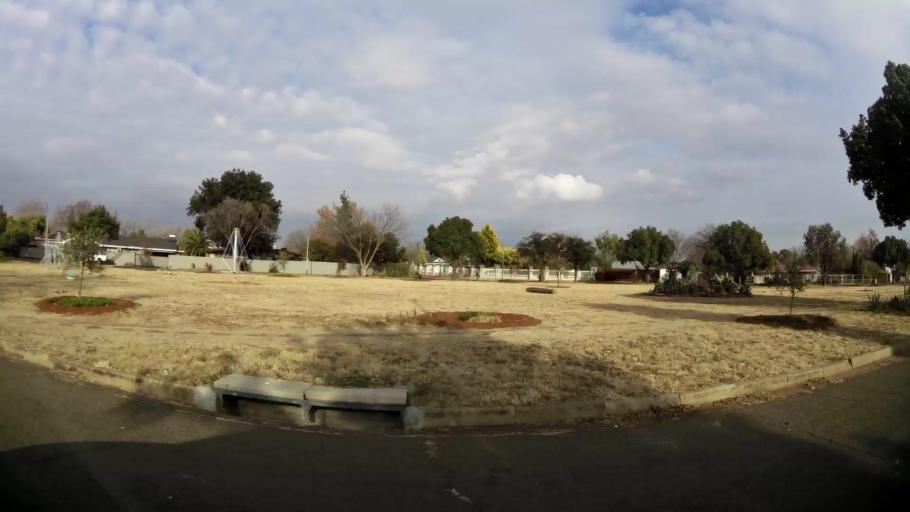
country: ZA
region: Orange Free State
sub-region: Mangaung Metropolitan Municipality
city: Bloemfontein
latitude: -29.1220
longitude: 26.1760
